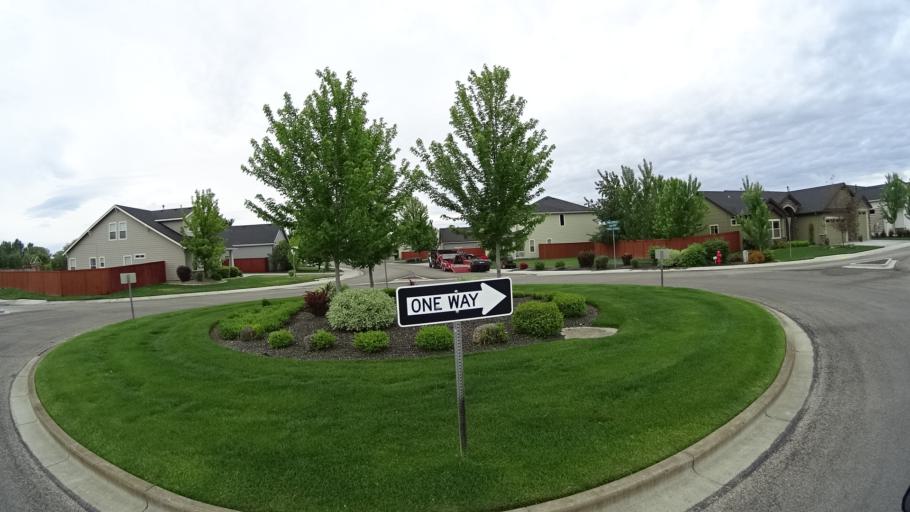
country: US
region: Idaho
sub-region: Ada County
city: Star
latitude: 43.7013
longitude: -116.4789
